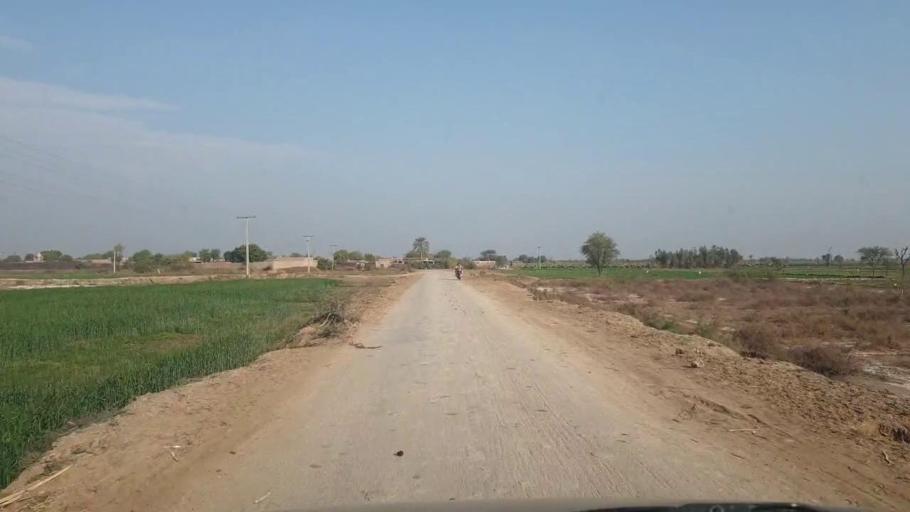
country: PK
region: Sindh
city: Tando Adam
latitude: 25.7444
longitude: 68.6070
